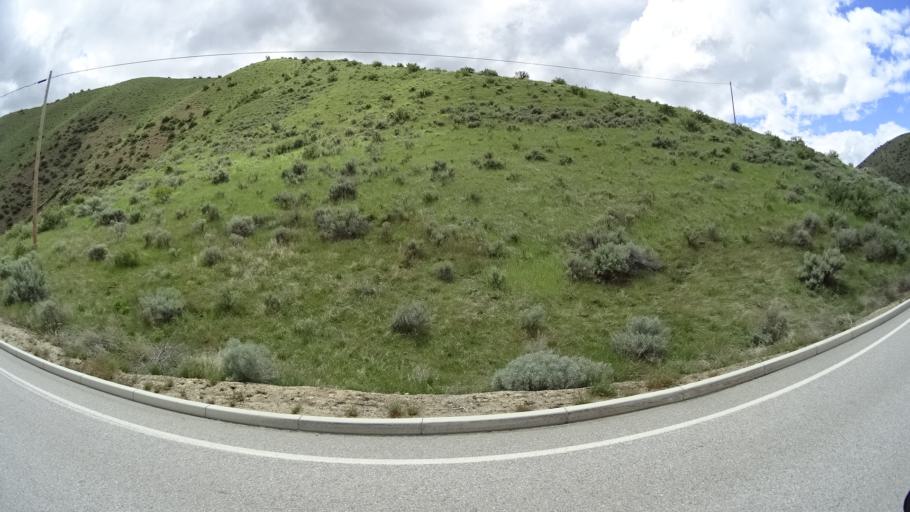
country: US
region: Idaho
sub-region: Ada County
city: Boise
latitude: 43.6871
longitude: -116.1830
